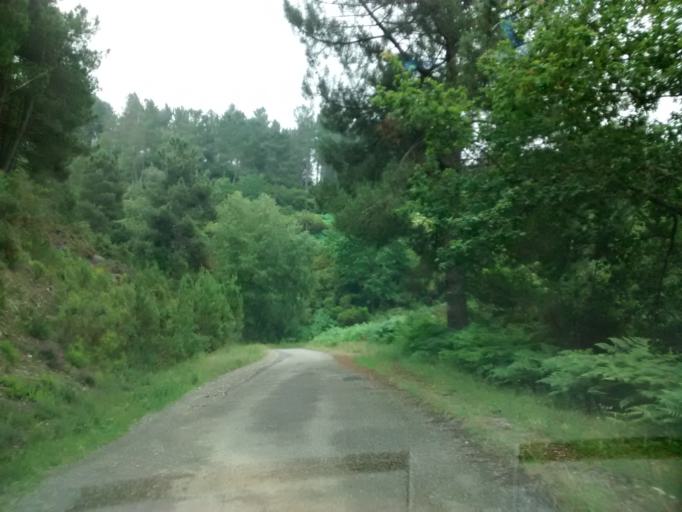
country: ES
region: Galicia
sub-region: Provincia de Ourense
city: Castro Caldelas
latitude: 42.4154
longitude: -7.3879
